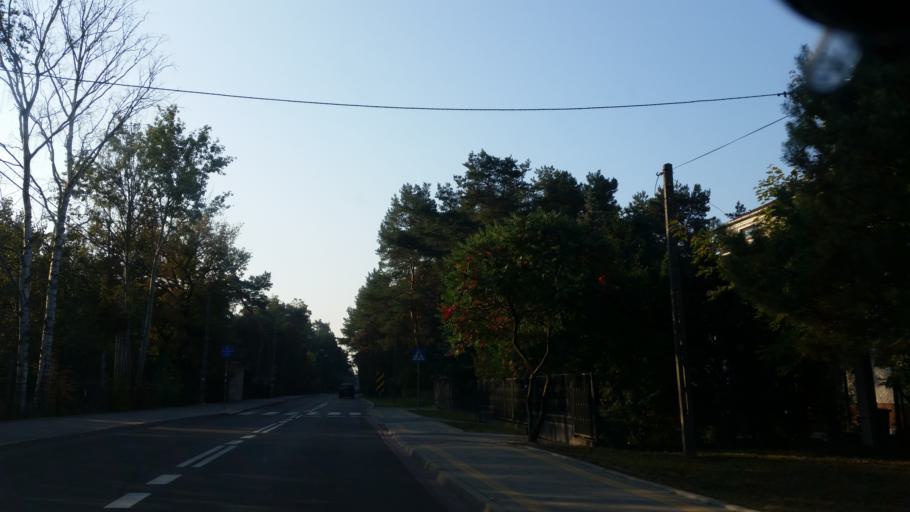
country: PL
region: Masovian Voivodeship
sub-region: Powiat otwocki
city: Jozefow
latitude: 52.1414
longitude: 21.2155
